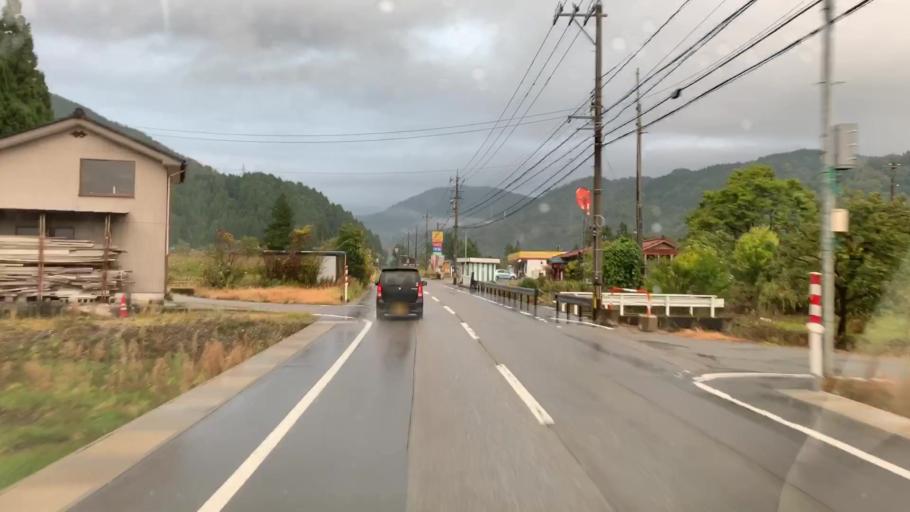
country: JP
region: Toyama
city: Kamiichi
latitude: 36.5855
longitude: 137.3333
